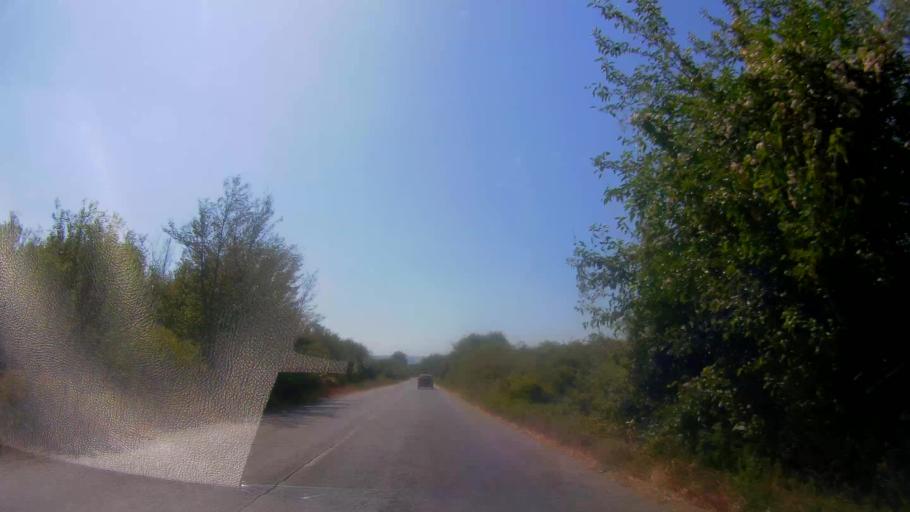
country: BG
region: Veliko Turnovo
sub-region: Obshtina Gorna Oryakhovitsa
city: Purvomaytsi
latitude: 43.2235
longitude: 25.6372
